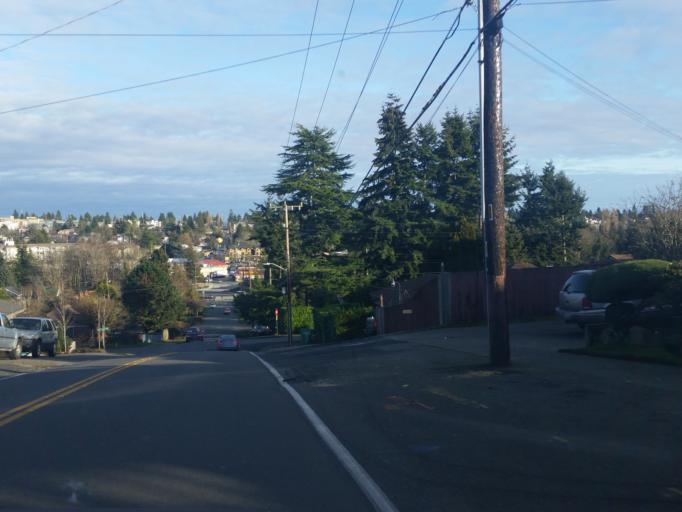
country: US
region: Washington
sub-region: King County
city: Shoreline
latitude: 47.7015
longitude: -122.3698
